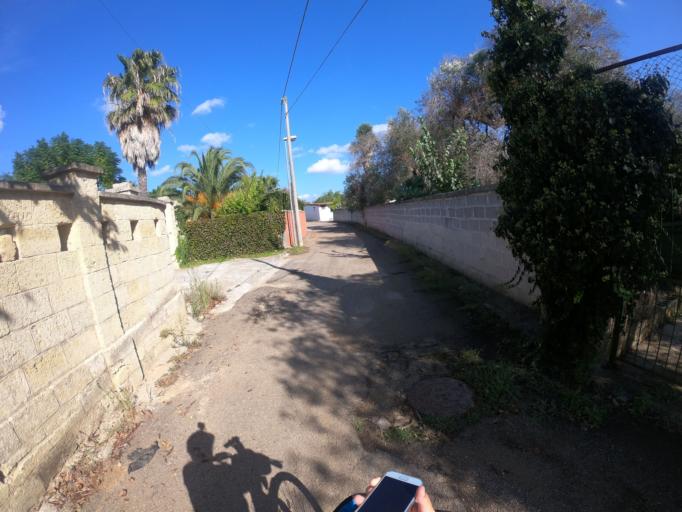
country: IT
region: Apulia
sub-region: Provincia di Lecce
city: Supersano
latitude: 40.0133
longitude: 18.2361
